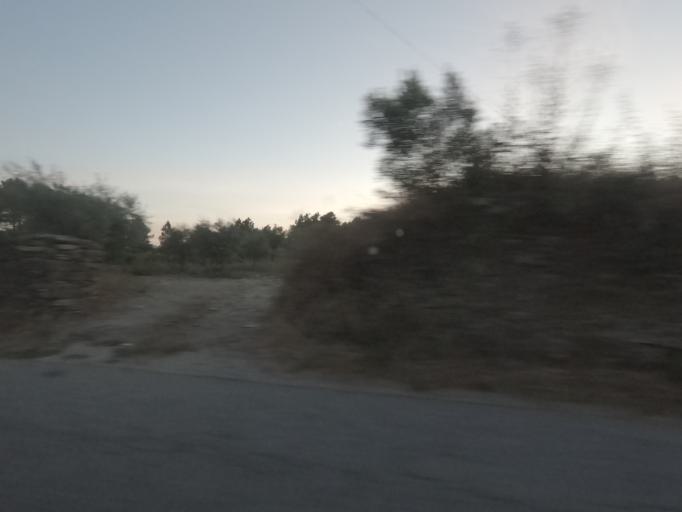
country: PT
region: Vila Real
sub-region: Peso da Regua
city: Peso da Regua
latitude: 41.1932
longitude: -7.7091
